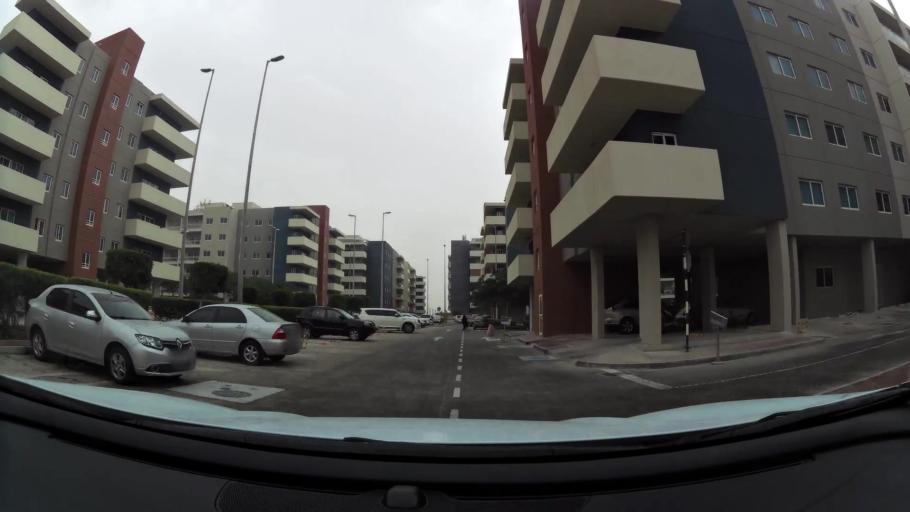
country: AE
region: Abu Dhabi
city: Abu Dhabi
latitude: 24.4551
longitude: 54.6727
